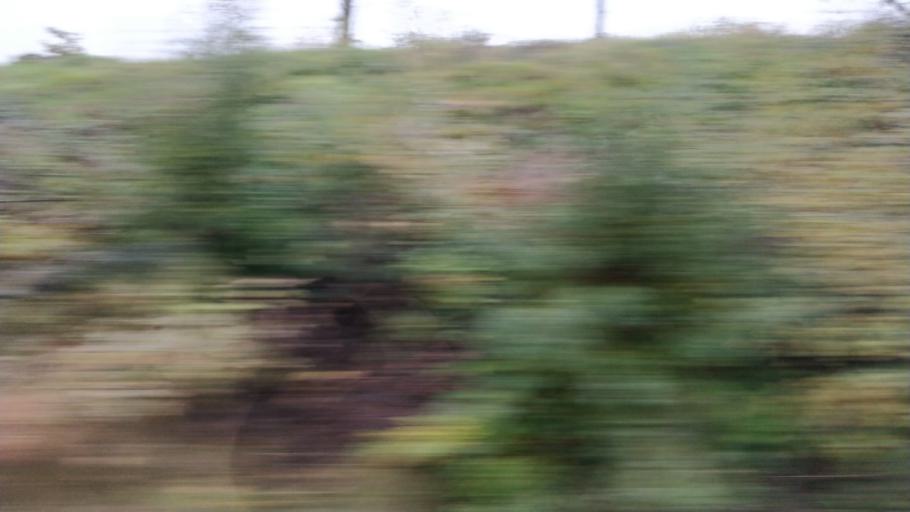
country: GB
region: England
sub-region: Borough of Bolton
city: Westhoughton
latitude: 53.5383
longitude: -2.5098
